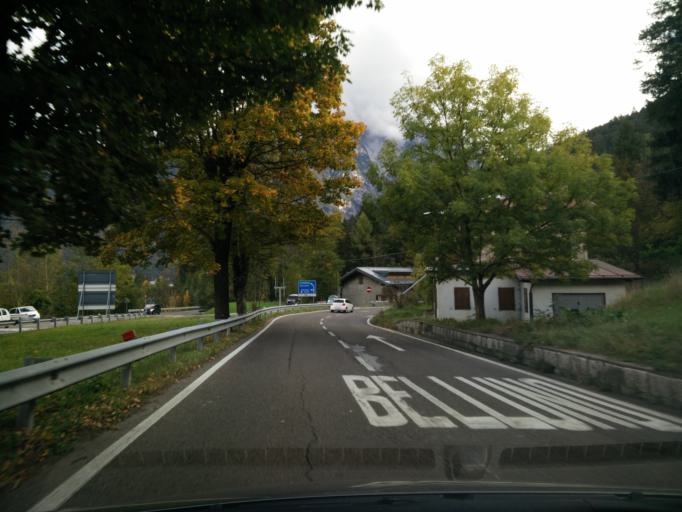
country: IT
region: Veneto
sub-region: Provincia di Belluno
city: Pieve di Cadore
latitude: 46.4221
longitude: 12.3659
